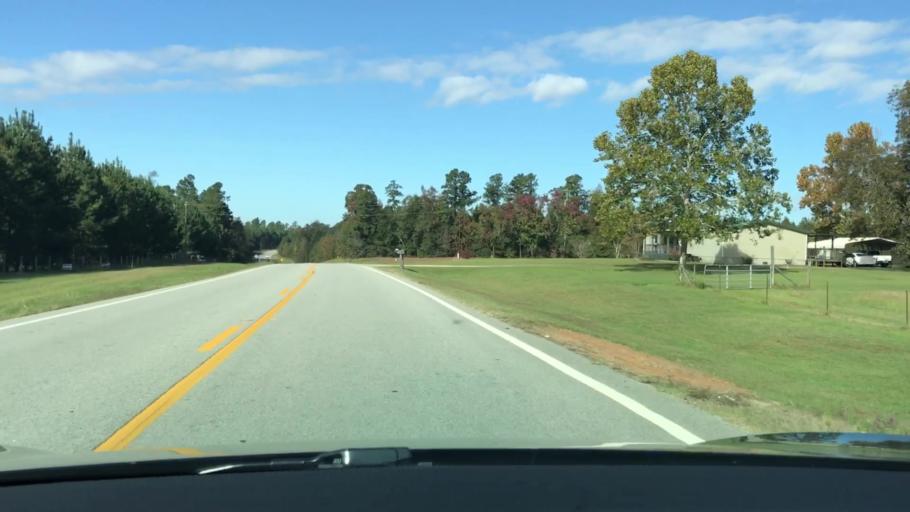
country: US
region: Georgia
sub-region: Jefferson County
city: Wrens
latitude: 33.2629
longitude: -82.4826
